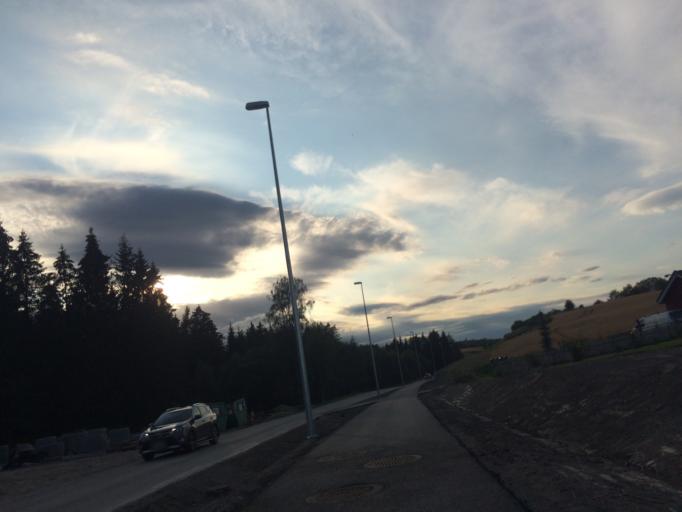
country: NO
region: Akershus
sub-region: Ski
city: Ski
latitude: 59.6841
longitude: 10.8735
